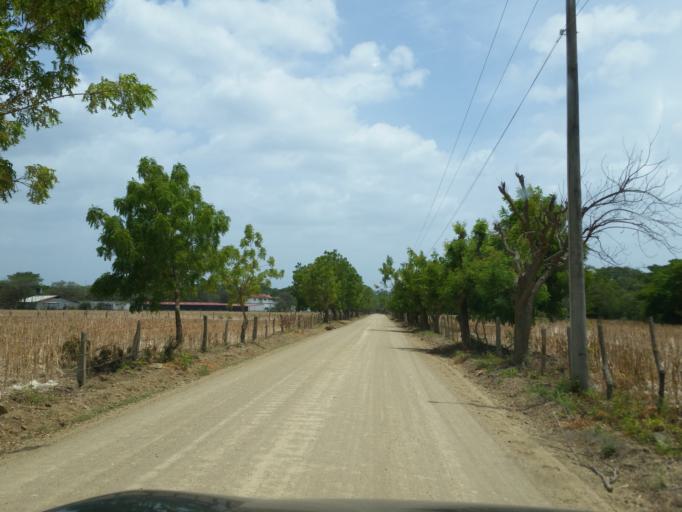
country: NI
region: Rivas
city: Tola
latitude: 11.4167
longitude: -86.0442
